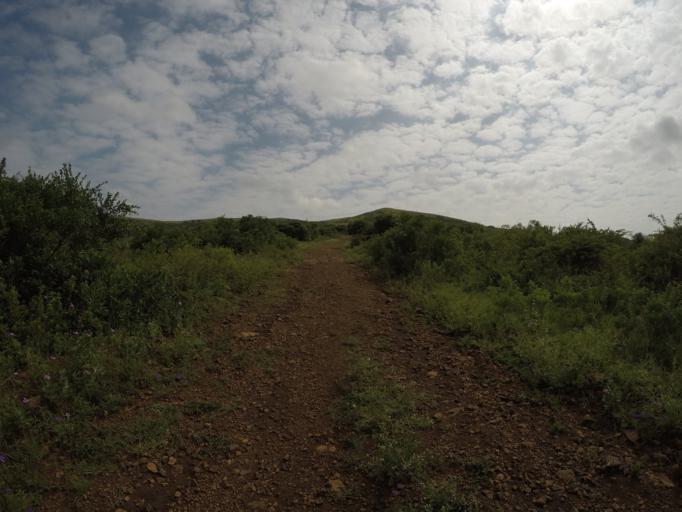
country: ZA
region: KwaZulu-Natal
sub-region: uThungulu District Municipality
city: Empangeni
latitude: -28.6133
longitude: 31.9048
